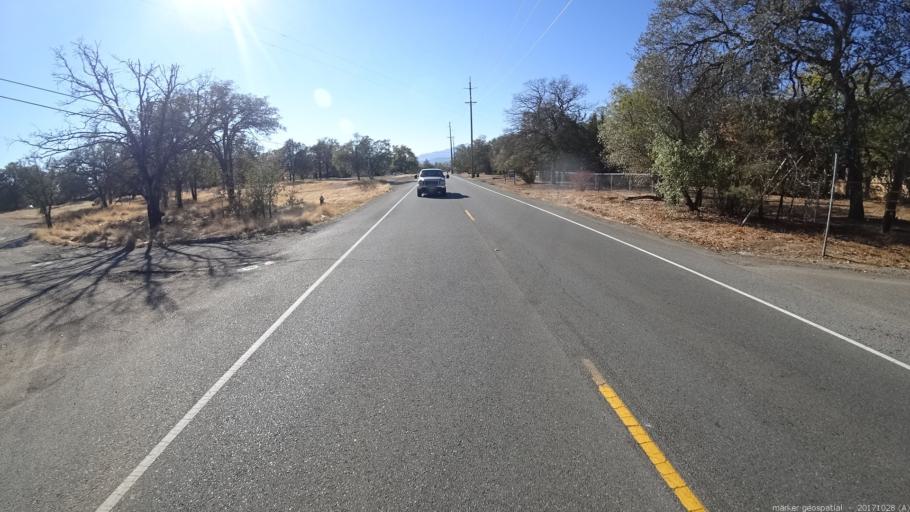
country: US
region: California
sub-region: Shasta County
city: Redding
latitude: 40.6323
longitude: -122.3937
